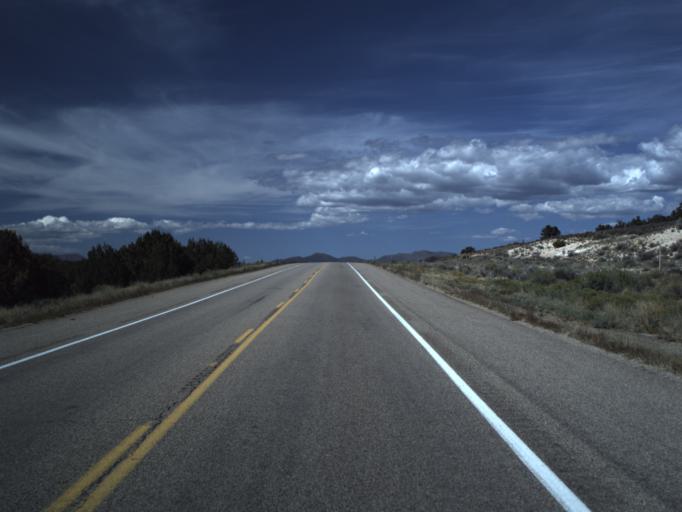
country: US
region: Utah
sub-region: Washington County
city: Ivins
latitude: 37.2733
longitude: -113.6443
